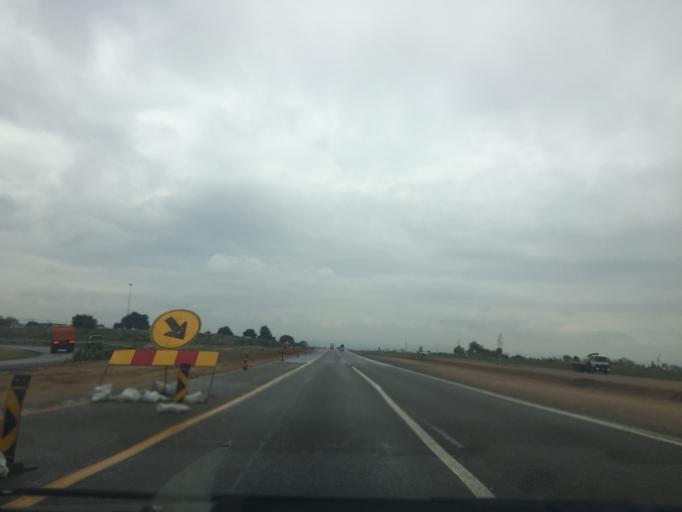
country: ZA
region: Gauteng
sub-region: City of Johannesburg Metropolitan Municipality
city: Diepsloot
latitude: -25.9150
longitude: 28.0240
